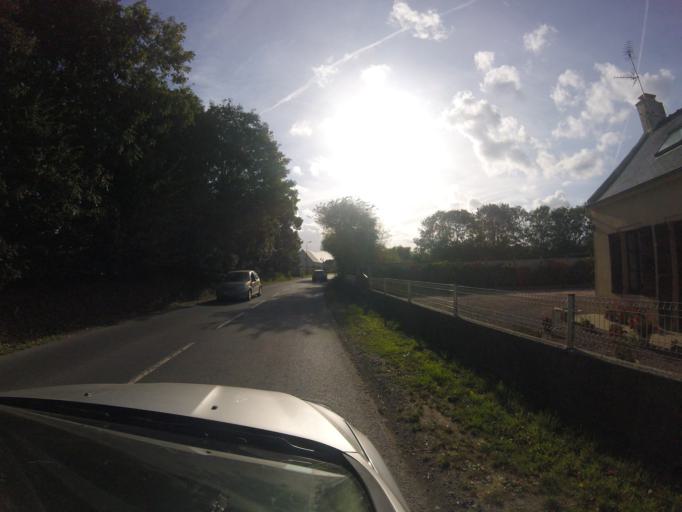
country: FR
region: Lower Normandy
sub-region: Departement du Calvados
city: Port-en-Bessin-Huppain
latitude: 49.3479
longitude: -0.8496
